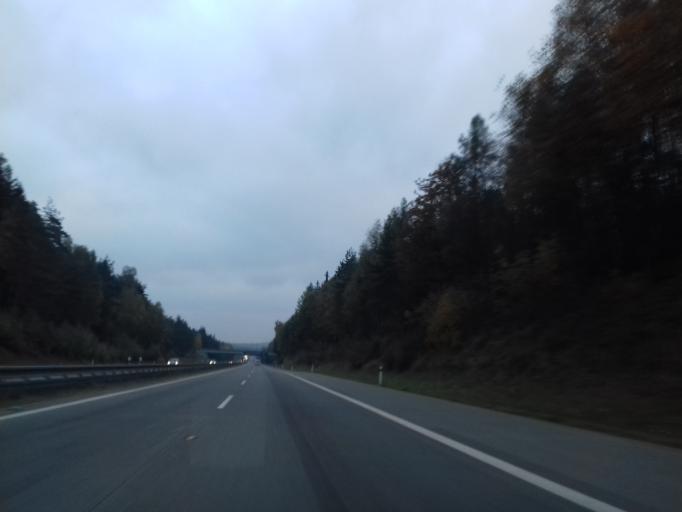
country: CZ
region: Central Bohemia
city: Cechtice
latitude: 49.6296
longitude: 15.1299
